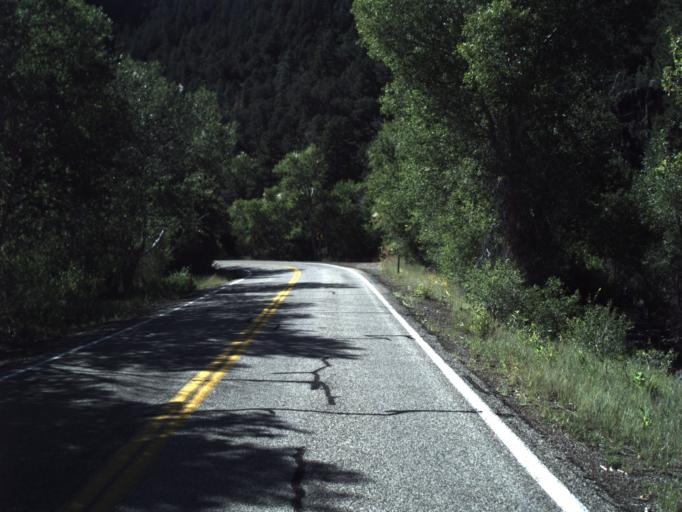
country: US
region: Utah
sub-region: Beaver County
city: Beaver
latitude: 38.2528
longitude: -112.5388
